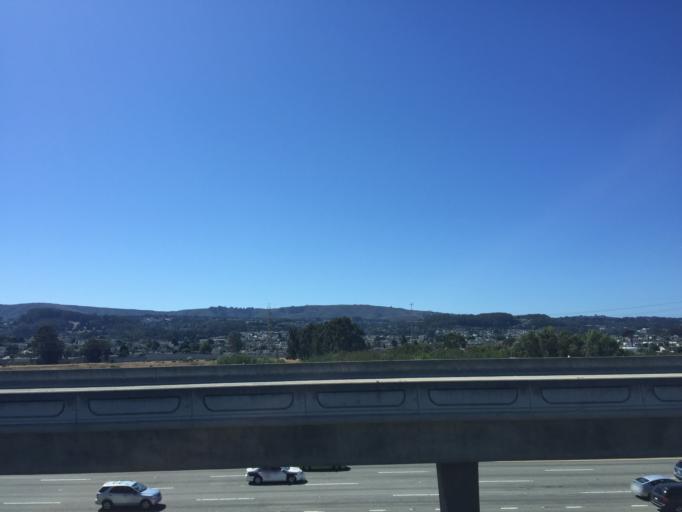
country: US
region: California
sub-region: San Mateo County
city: San Bruno
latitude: 37.6235
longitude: -122.4001
